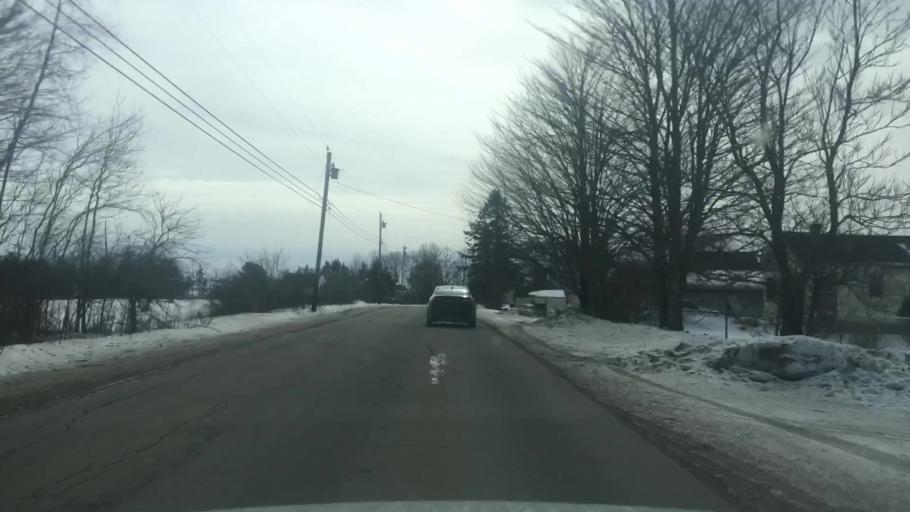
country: US
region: Maine
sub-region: Hancock County
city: Orland
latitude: 44.5796
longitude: -68.7254
